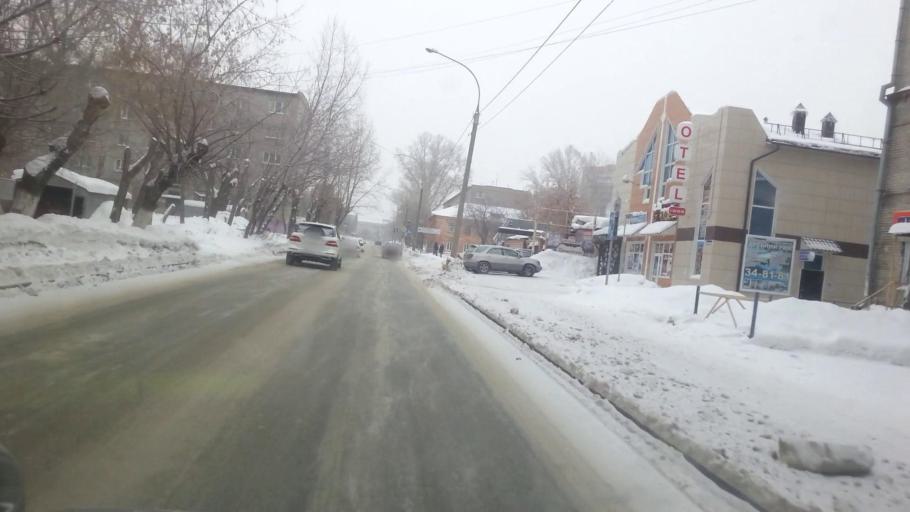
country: RU
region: Altai Krai
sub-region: Gorod Barnaulskiy
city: Barnaul
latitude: 53.3808
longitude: 83.7333
